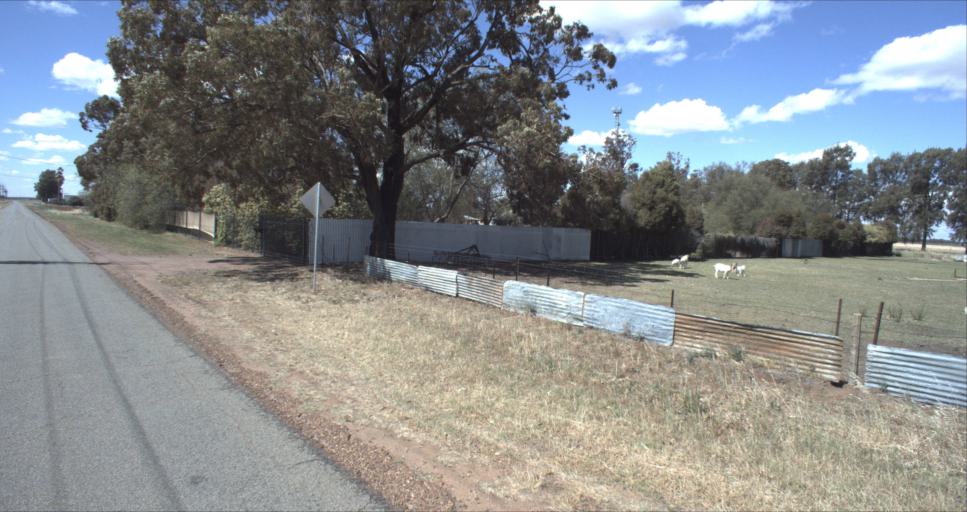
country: AU
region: New South Wales
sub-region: Leeton
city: Leeton
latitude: -34.5145
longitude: 146.2511
